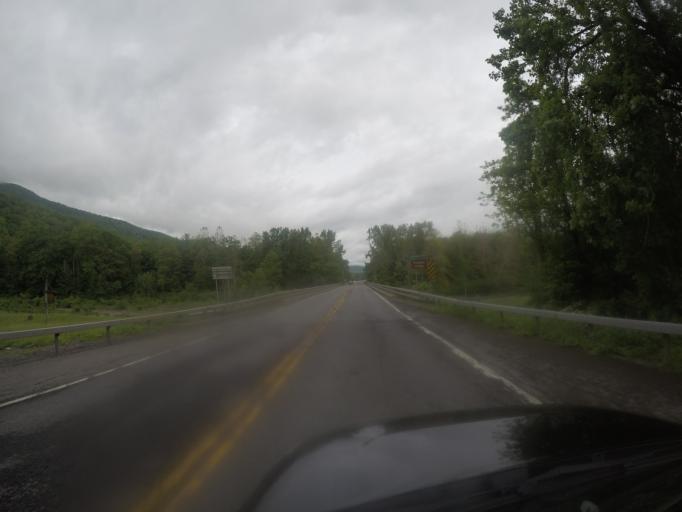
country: US
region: New York
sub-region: Ulster County
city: Shokan
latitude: 42.0407
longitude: -74.2802
